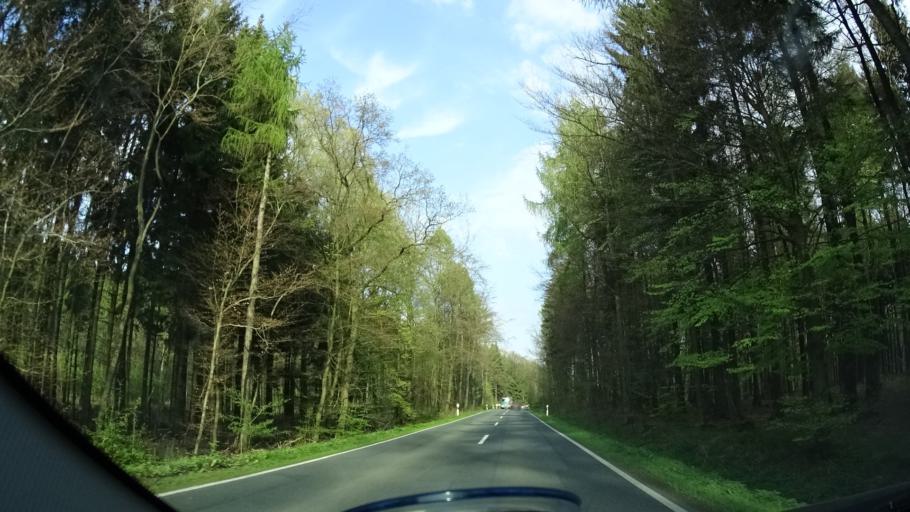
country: DE
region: North Rhine-Westphalia
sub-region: Regierungsbezirk Detmold
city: Buren
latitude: 51.5620
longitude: 8.6280
